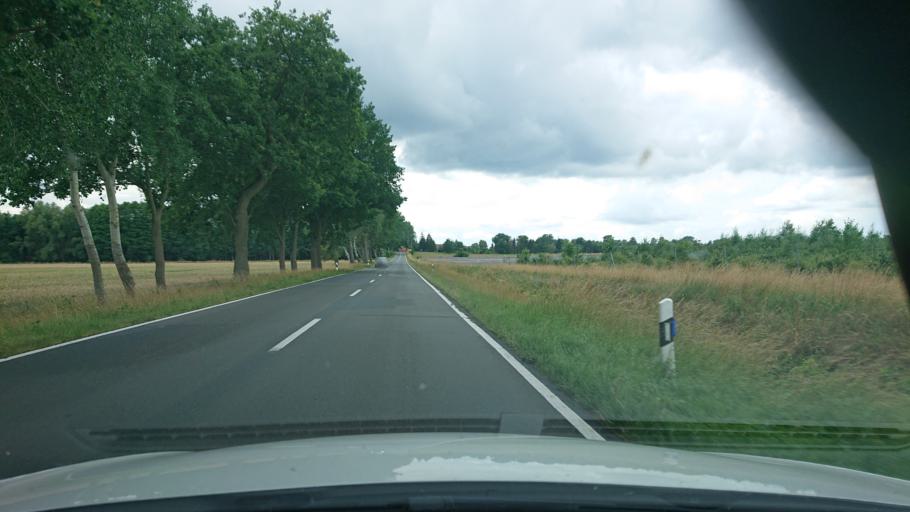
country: DE
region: Mecklenburg-Vorpommern
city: Ludwigslust
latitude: 53.3470
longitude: 11.4211
